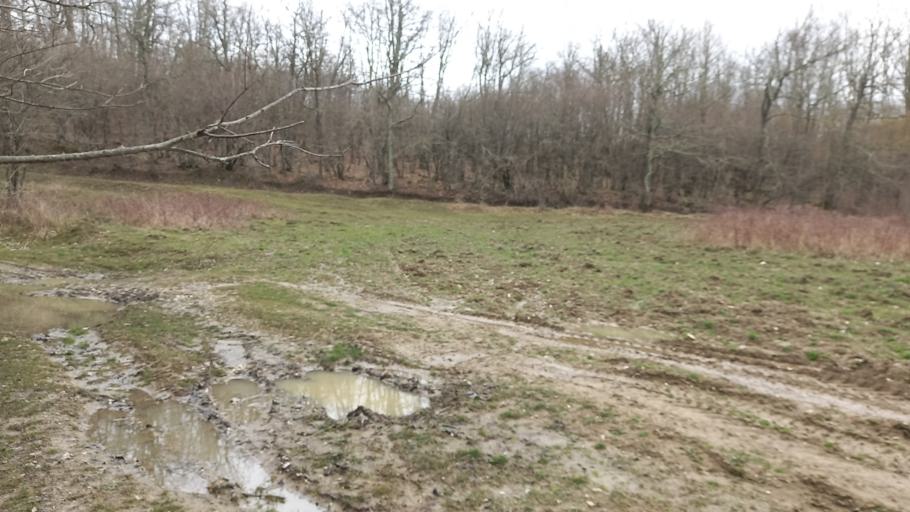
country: RU
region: Krasnodarskiy
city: Pshada
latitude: 44.4832
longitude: 38.4014
